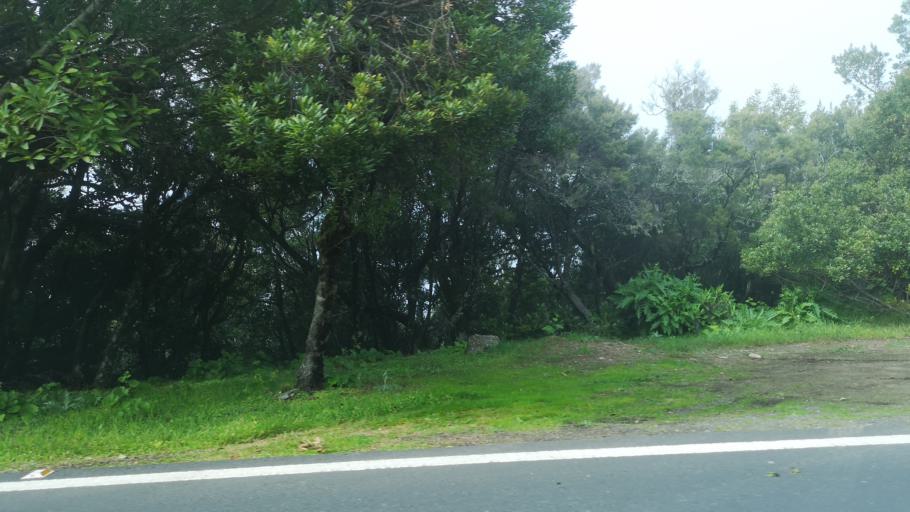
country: ES
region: Canary Islands
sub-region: Provincia de Santa Cruz de Tenerife
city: Alajero
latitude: 28.1075
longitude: -17.2370
